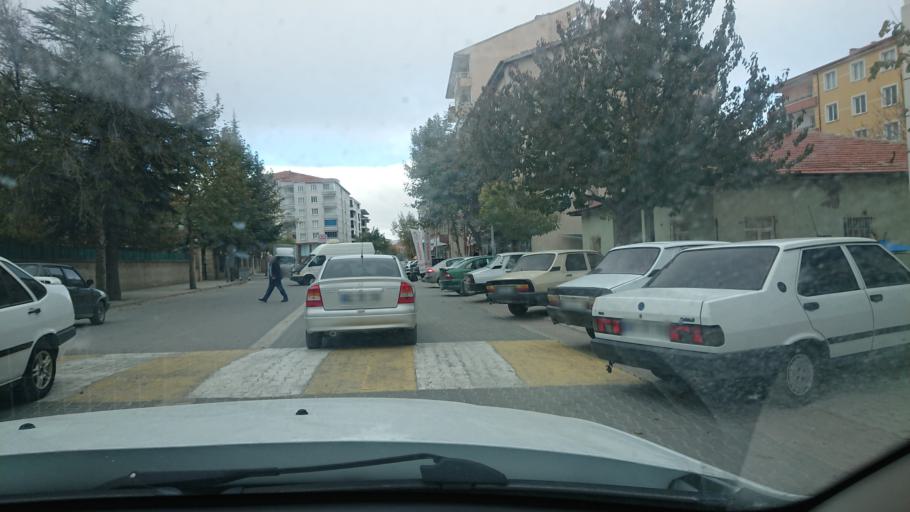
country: TR
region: Aksaray
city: Ortakoy
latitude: 38.7379
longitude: 34.0386
